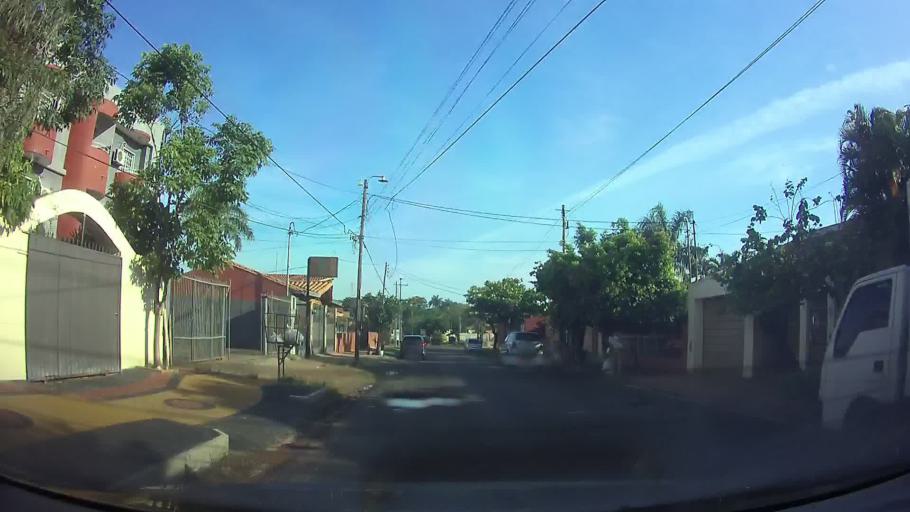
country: PY
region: Central
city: San Lorenzo
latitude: -25.2646
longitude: -57.5016
